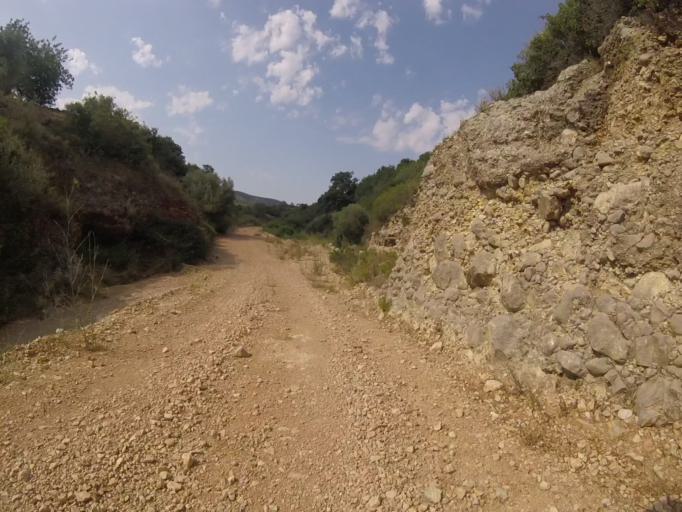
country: ES
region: Valencia
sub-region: Provincia de Castello
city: Alcala de Xivert
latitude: 40.3332
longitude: 0.1939
